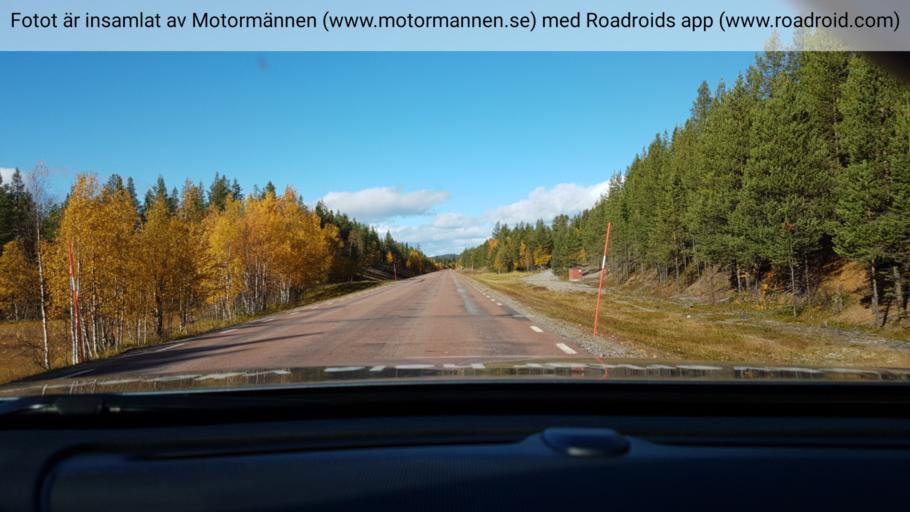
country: SE
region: Norrbotten
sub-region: Arjeplogs Kommun
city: Arjeplog
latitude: 66.0079
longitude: 18.1025
